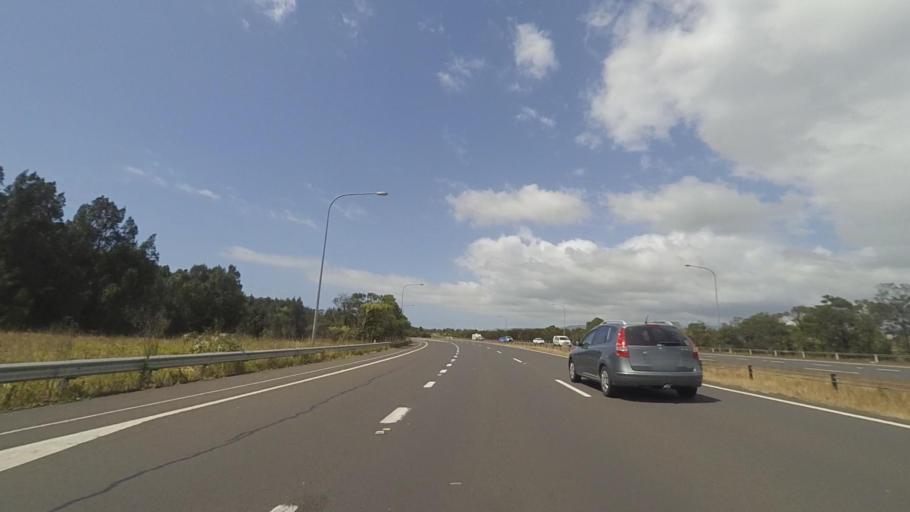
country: AU
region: New South Wales
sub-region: Shellharbour
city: Croom
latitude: -34.6123
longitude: 150.8372
